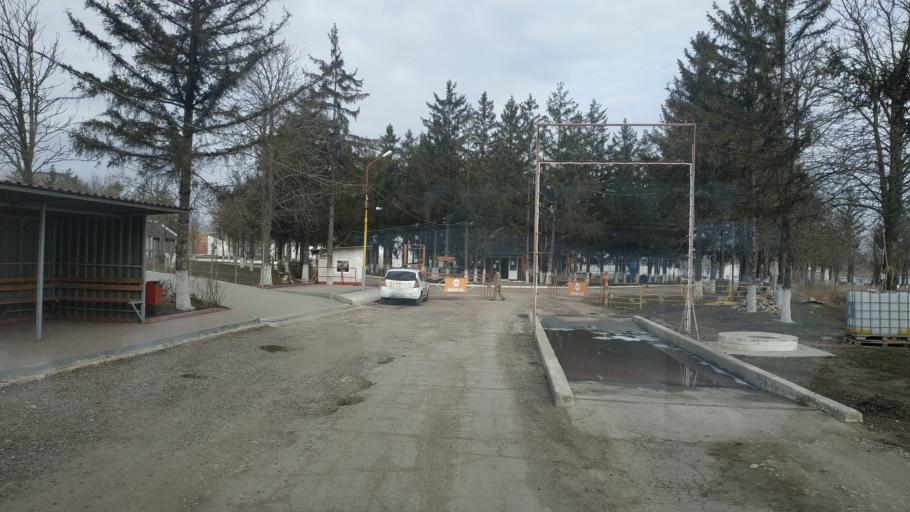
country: MD
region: Chisinau
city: Vadul lui Voda
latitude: 46.9948
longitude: 29.1043
